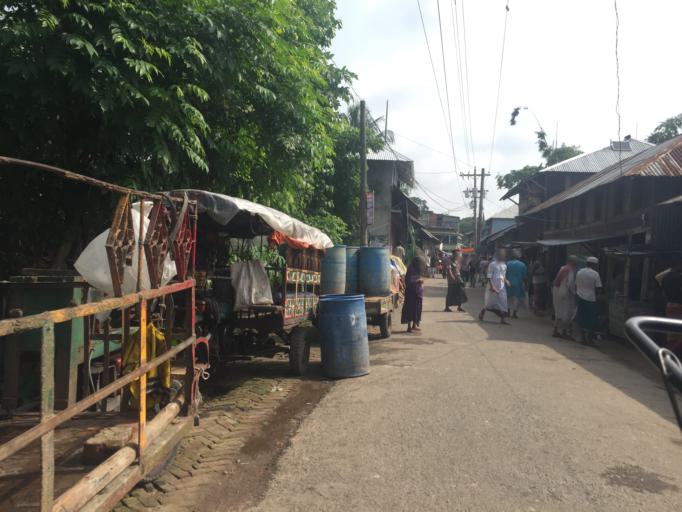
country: BD
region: Barisal
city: Mathba
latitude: 22.2441
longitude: 89.9142
